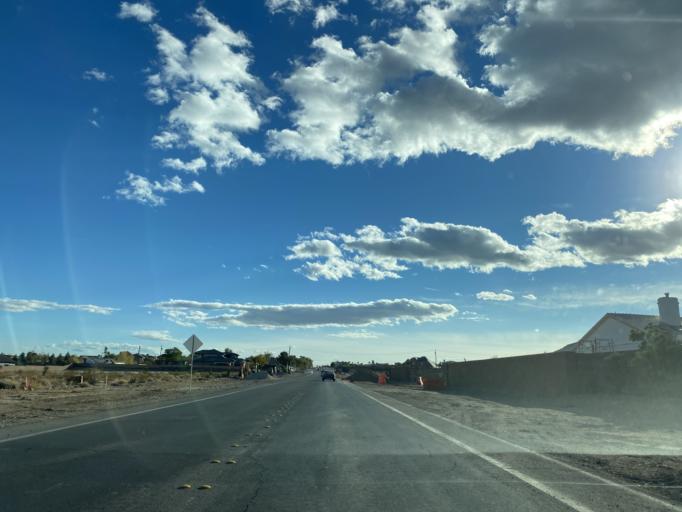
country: US
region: Nevada
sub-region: Clark County
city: Summerlin South
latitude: 36.2403
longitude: -115.2975
